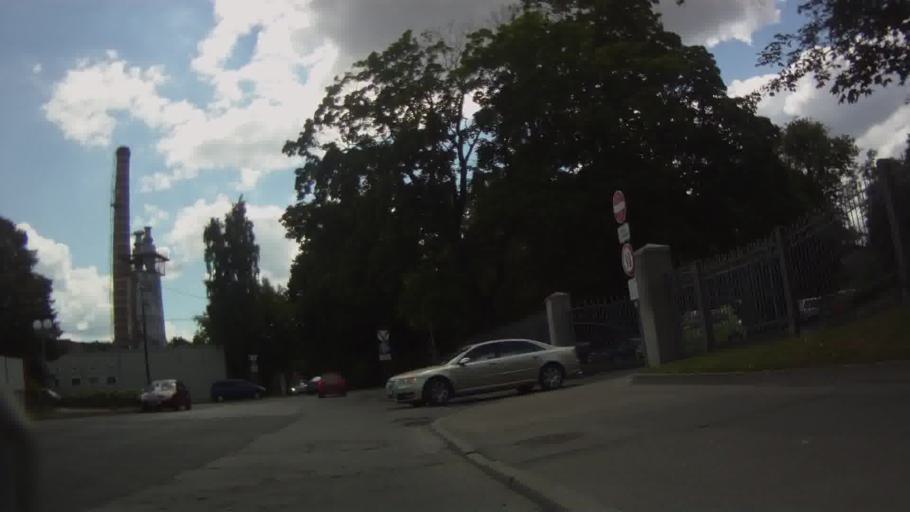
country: LV
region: Riga
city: Riga
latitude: 56.9176
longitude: 24.1062
